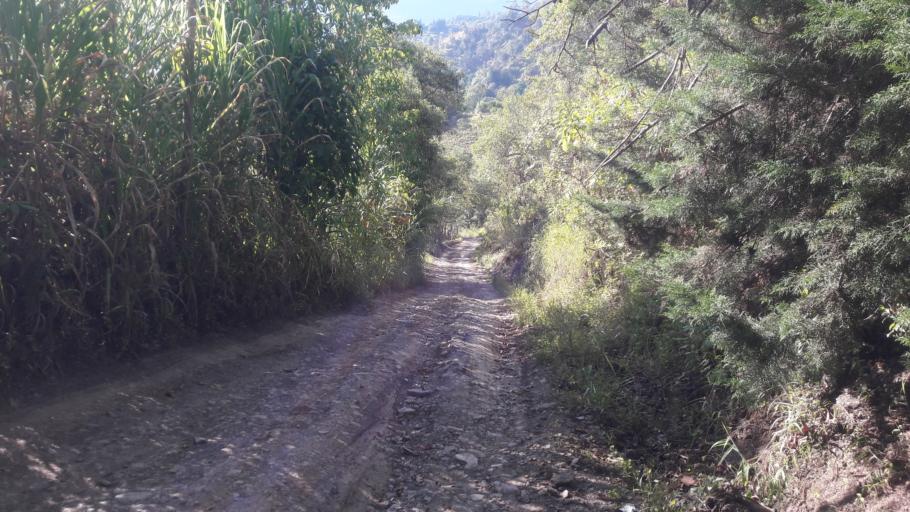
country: CO
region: Cundinamarca
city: Tenza
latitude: 5.0862
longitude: -73.4170
